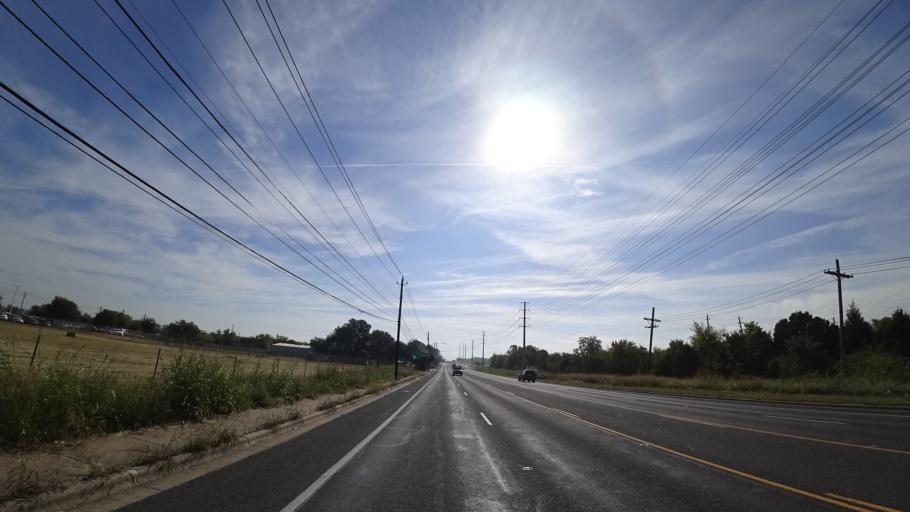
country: US
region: Texas
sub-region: Travis County
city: Austin
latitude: 30.2093
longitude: -97.7243
